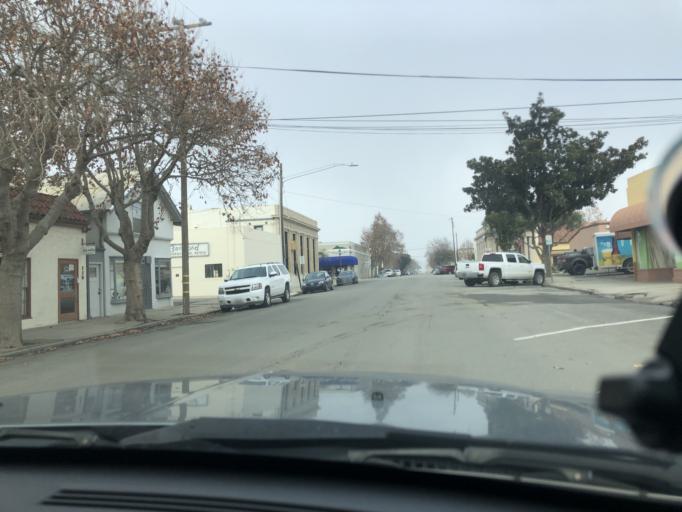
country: US
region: California
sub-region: Monterey County
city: King City
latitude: 36.2123
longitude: -121.1259
